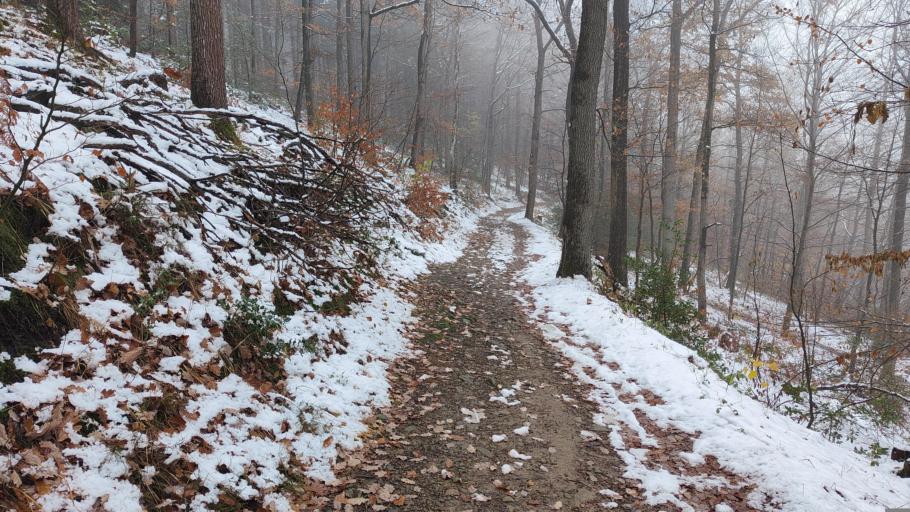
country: BE
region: Wallonia
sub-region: Province de Liege
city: Eupen
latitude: 50.6232
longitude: 6.0667
